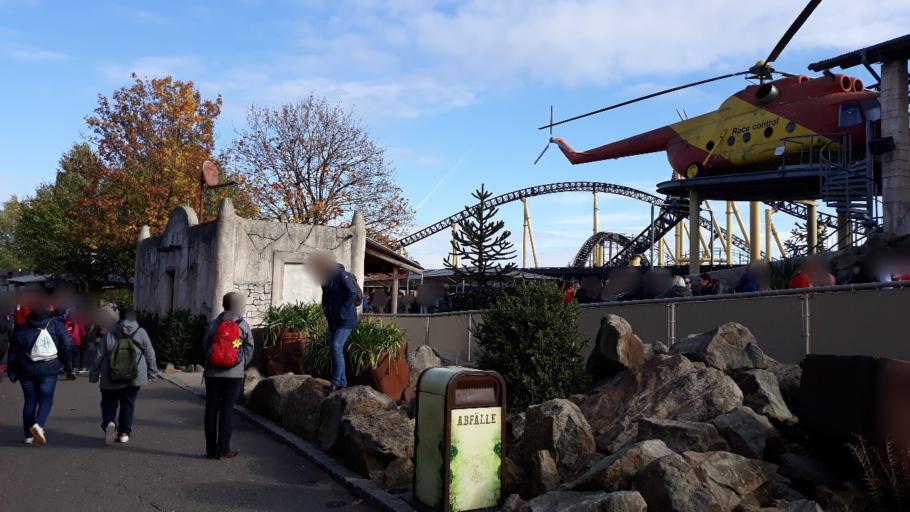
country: DE
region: Lower Saxony
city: Soltau
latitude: 53.0219
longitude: 9.8806
